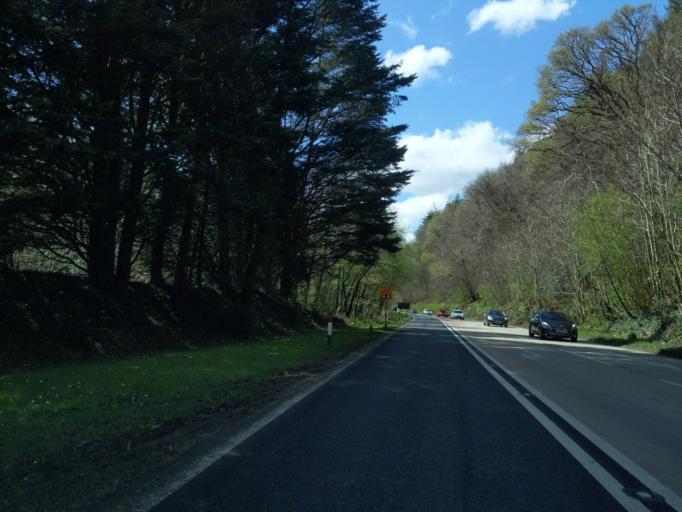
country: GB
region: England
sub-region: Cornwall
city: Liskeard
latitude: 50.4558
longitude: -4.5675
